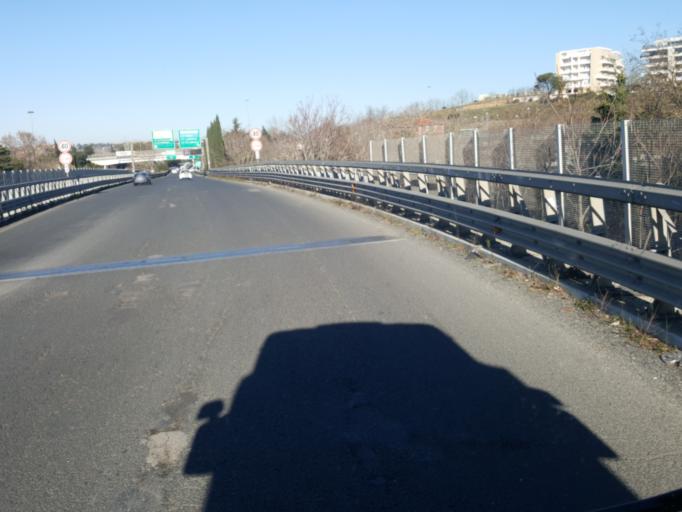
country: IT
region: Latium
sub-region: Citta metropolitana di Roma Capitale
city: Vitinia
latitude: 41.8032
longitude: 12.4191
